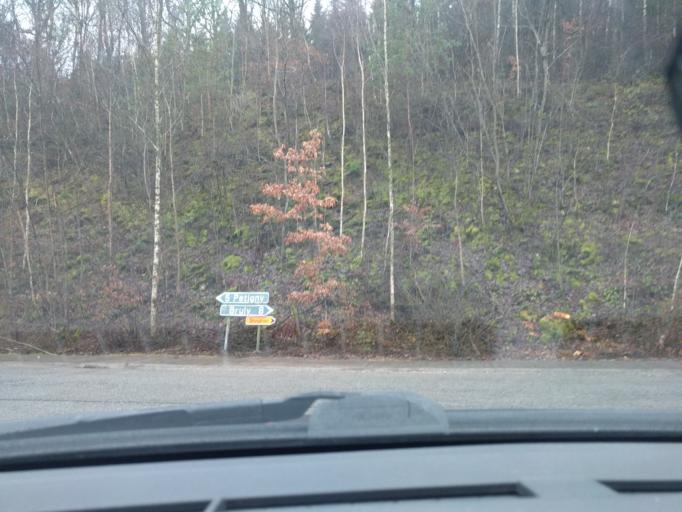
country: BE
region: Wallonia
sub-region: Province de Namur
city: Couvin
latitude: 50.0236
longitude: 4.5333
